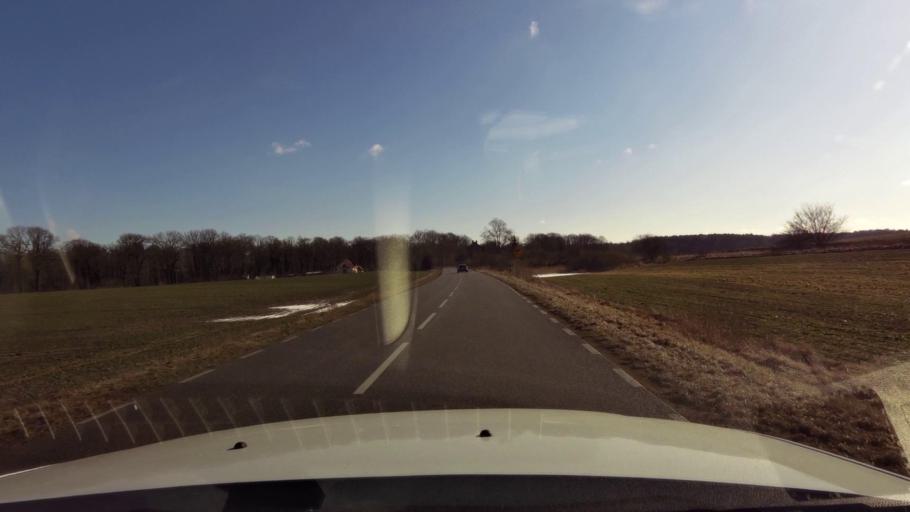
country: PL
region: West Pomeranian Voivodeship
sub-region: Powiat mysliborski
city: Barlinek
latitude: 52.9856
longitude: 15.1176
